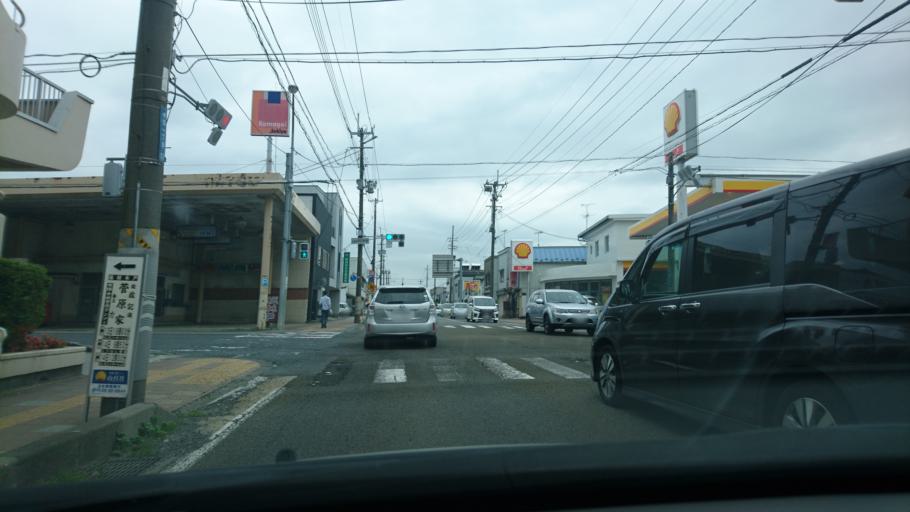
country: JP
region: Miyagi
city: Furukawa
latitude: 38.7351
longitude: 141.0224
